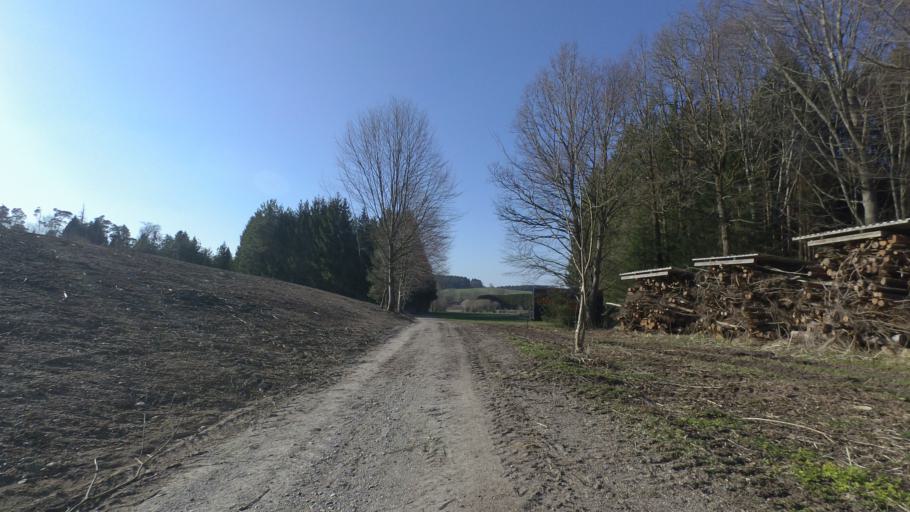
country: DE
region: Bavaria
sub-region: Upper Bavaria
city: Chieming
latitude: 47.9394
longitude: 12.5483
